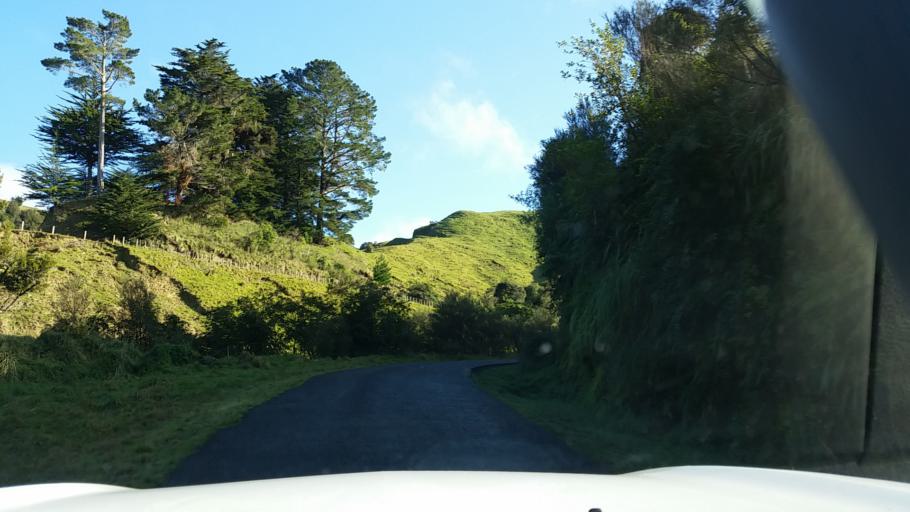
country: NZ
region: Taranaki
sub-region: South Taranaki District
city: Eltham
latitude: -39.5128
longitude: 174.3864
